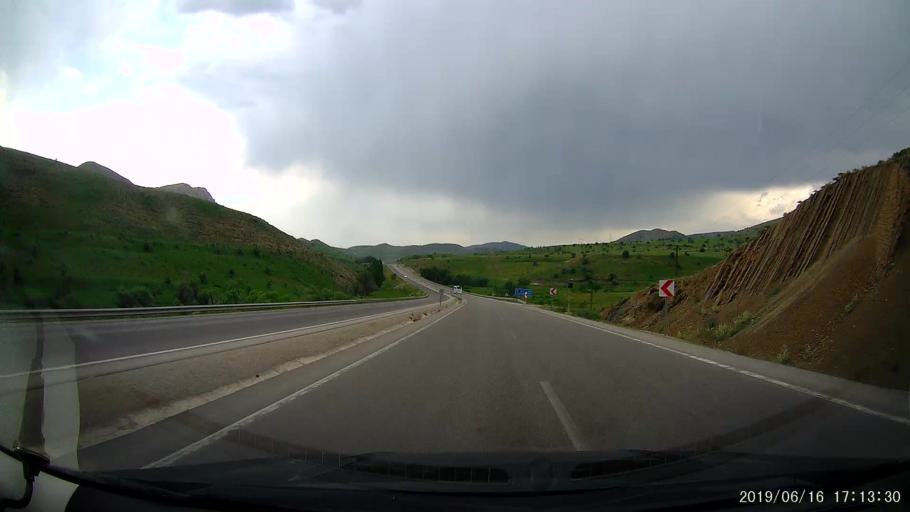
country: TR
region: Erzurum
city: Askale
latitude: 39.8592
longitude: 40.5969
